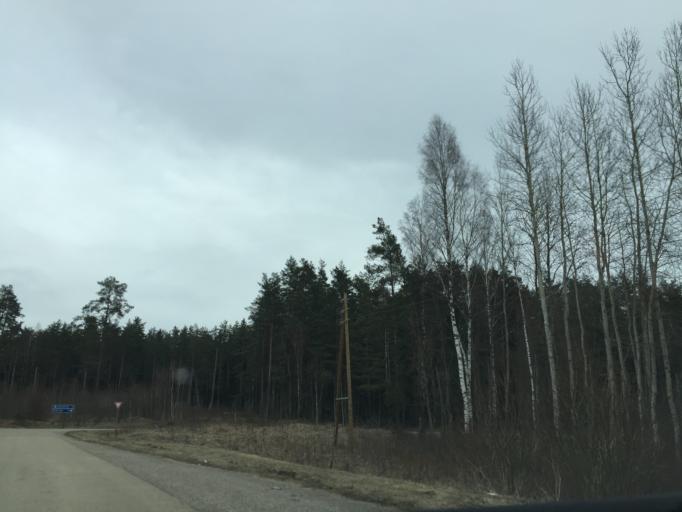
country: LV
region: Kraslavas Rajons
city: Kraslava
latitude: 55.9127
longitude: 26.9973
